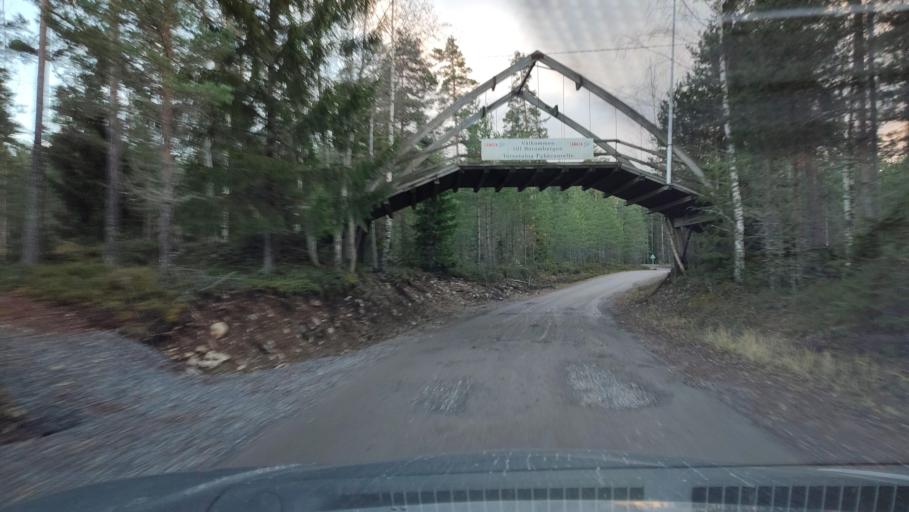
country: FI
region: Southern Ostrobothnia
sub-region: Suupohja
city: Karijoki
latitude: 62.2868
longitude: 21.6319
